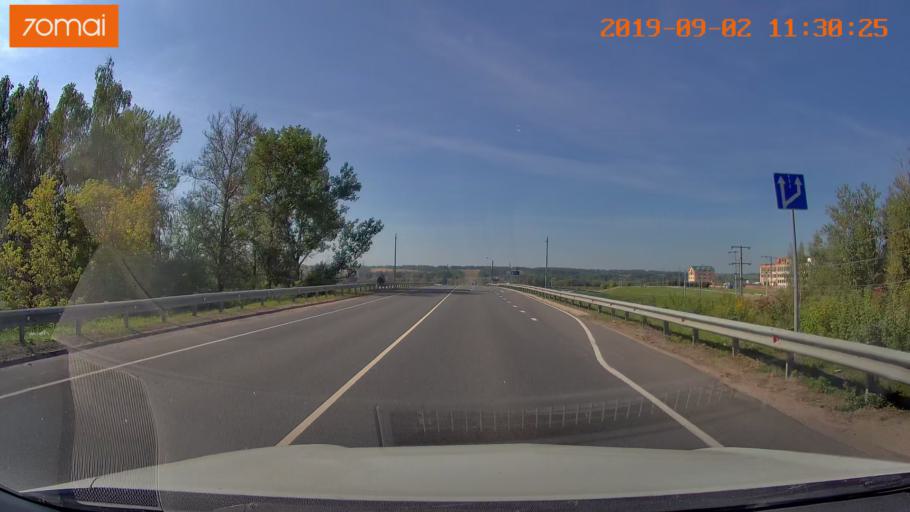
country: RU
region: Smolensk
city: Roslavl'
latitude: 53.9843
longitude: 32.8345
